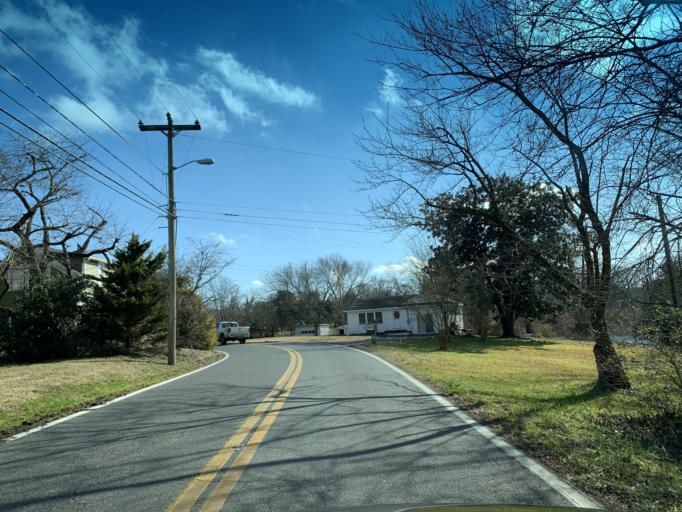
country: US
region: Delaware
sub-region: Sussex County
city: Selbyville
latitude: 38.4418
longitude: -75.1929
